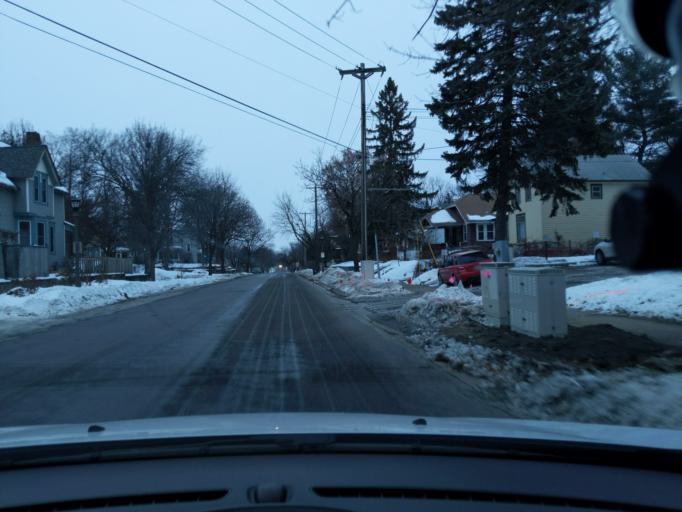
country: US
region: Minnesota
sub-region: Ramsey County
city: Falcon Heights
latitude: 44.9633
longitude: -93.1772
